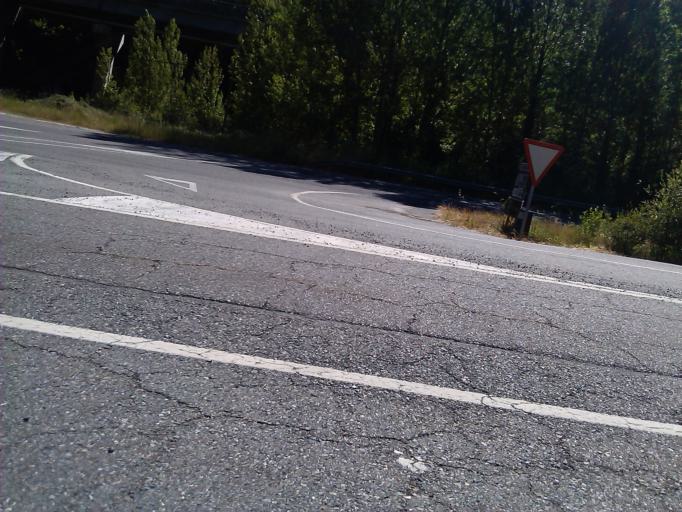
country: ES
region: Castille and Leon
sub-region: Provincia de Leon
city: Vega de Valcarce
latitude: 42.6621
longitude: -6.9261
